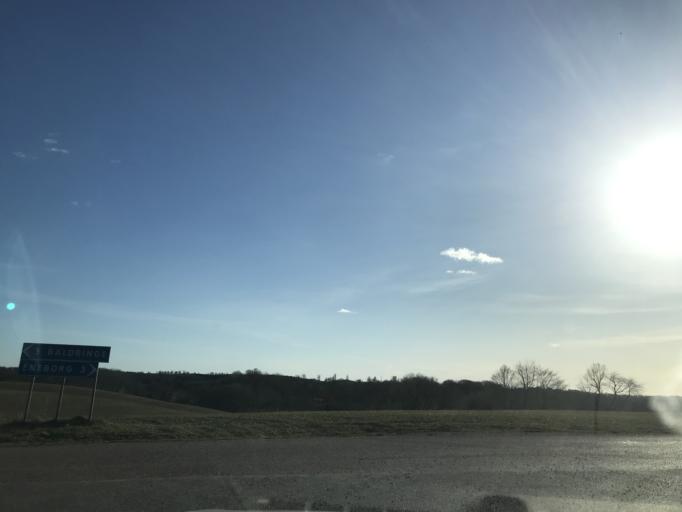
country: SE
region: Skane
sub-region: Ystads Kommun
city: Ystad
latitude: 55.5468
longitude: 13.8048
